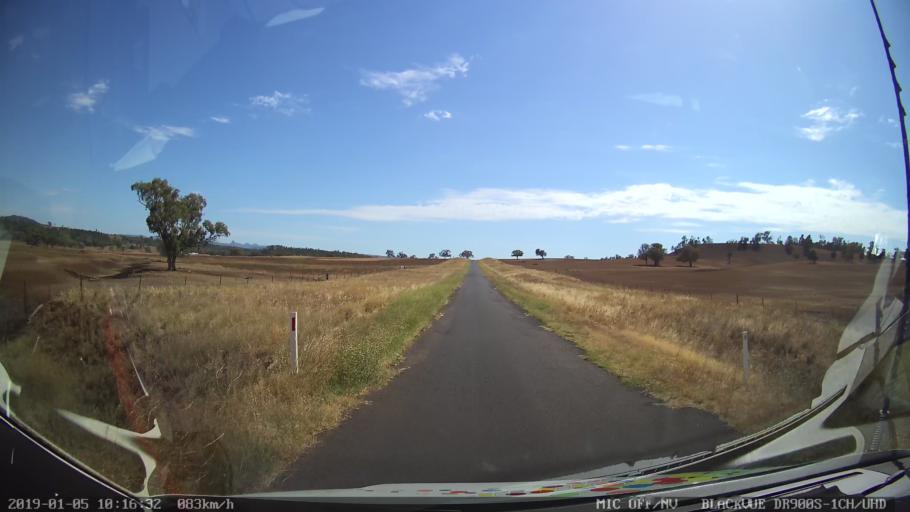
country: AU
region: New South Wales
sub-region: Gilgandra
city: Gilgandra
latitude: -31.5743
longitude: 148.9533
